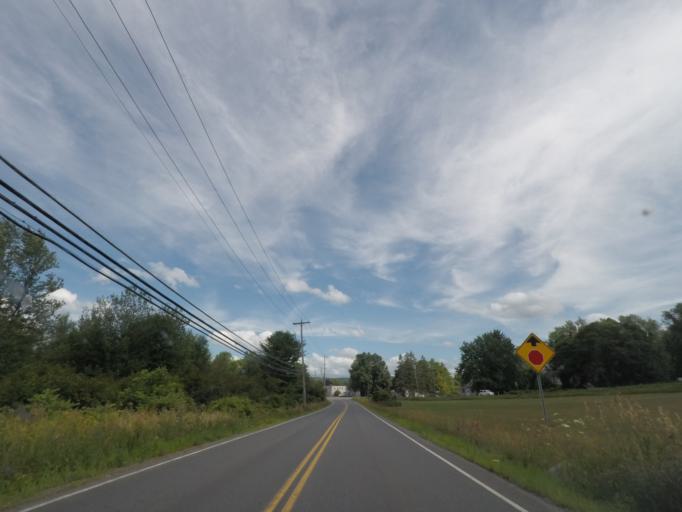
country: US
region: New York
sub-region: Rensselaer County
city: Poestenkill
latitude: 42.6940
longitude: -73.5979
